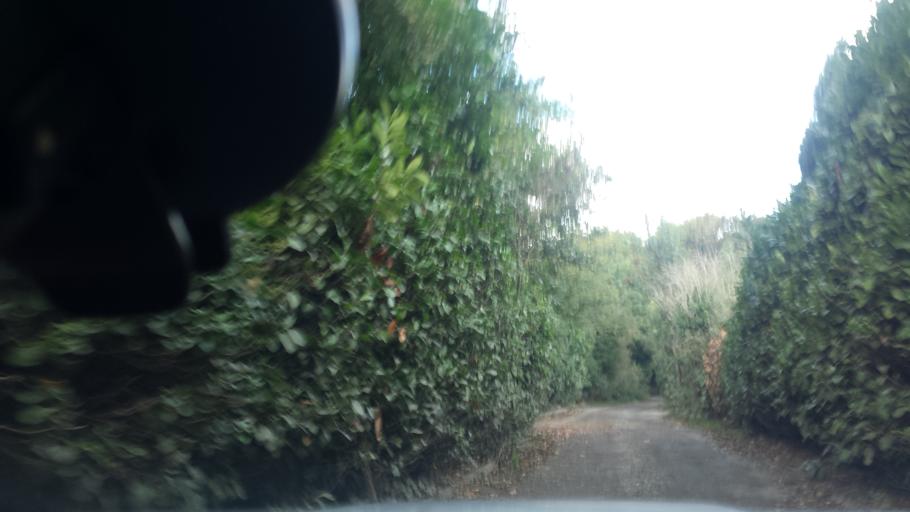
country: GB
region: England
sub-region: Kent
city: Swanley
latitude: 51.4155
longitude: 0.1819
